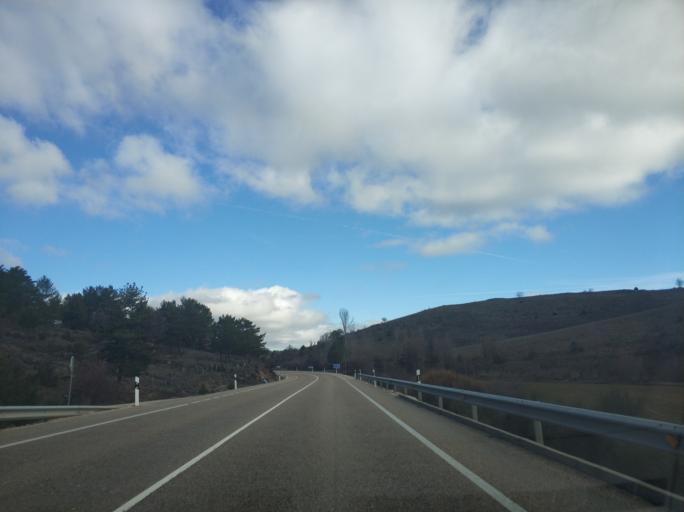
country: ES
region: Castille and Leon
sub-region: Provincia de Burgos
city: Rabanera del Pinar
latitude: 41.8754
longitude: -3.2213
